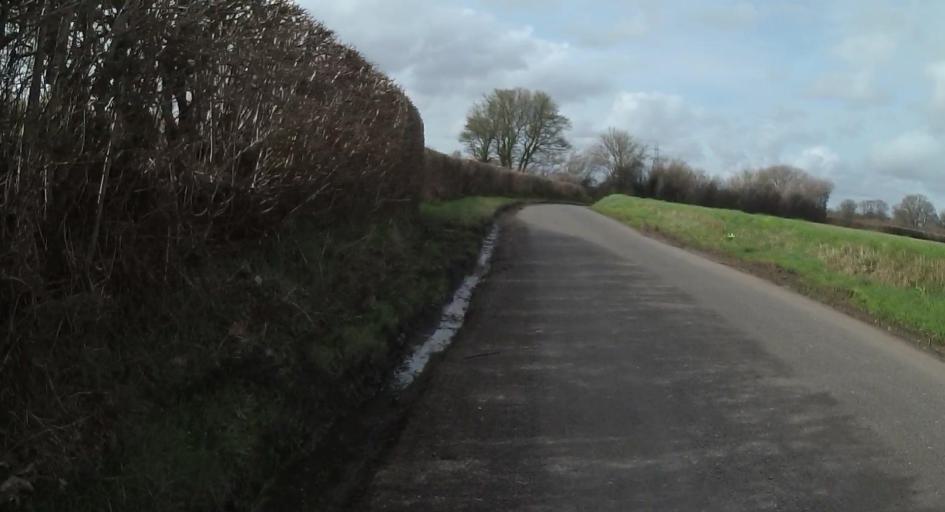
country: GB
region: England
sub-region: Hampshire
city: Kingsclere
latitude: 51.3342
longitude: -1.2453
